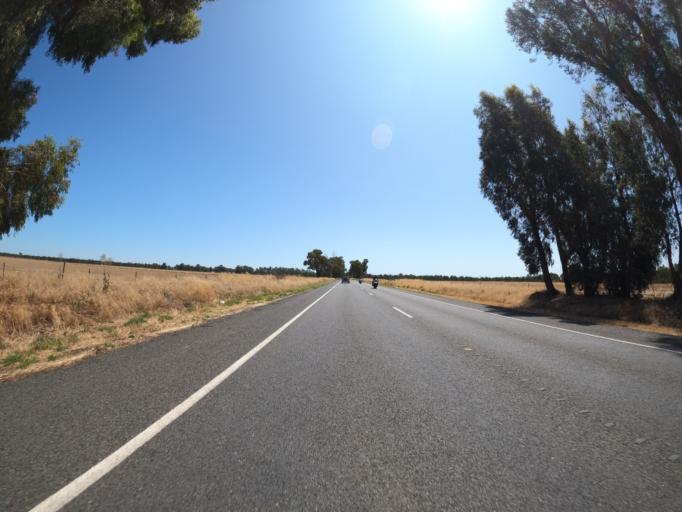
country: AU
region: Victoria
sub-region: Moira
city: Yarrawonga
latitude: -36.0225
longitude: 146.1338
